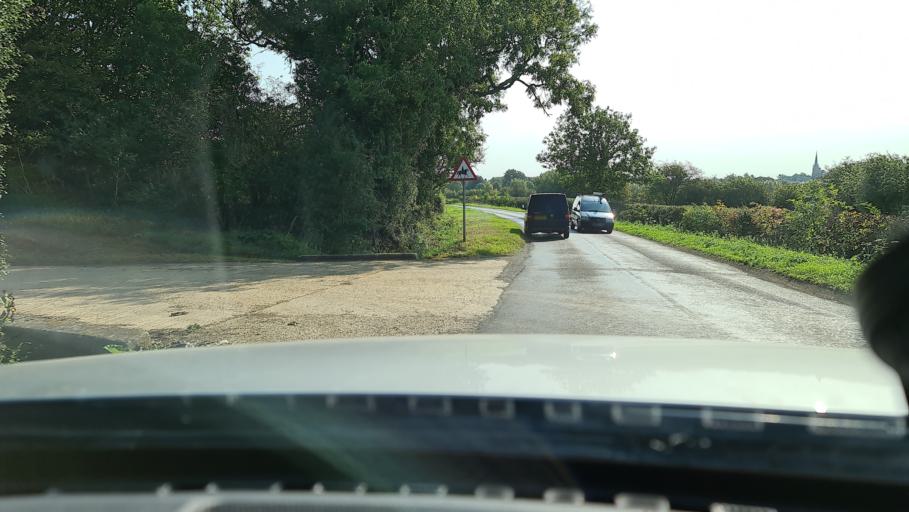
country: GB
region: England
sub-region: Oxfordshire
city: Adderbury
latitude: 52.0300
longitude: -1.2875
